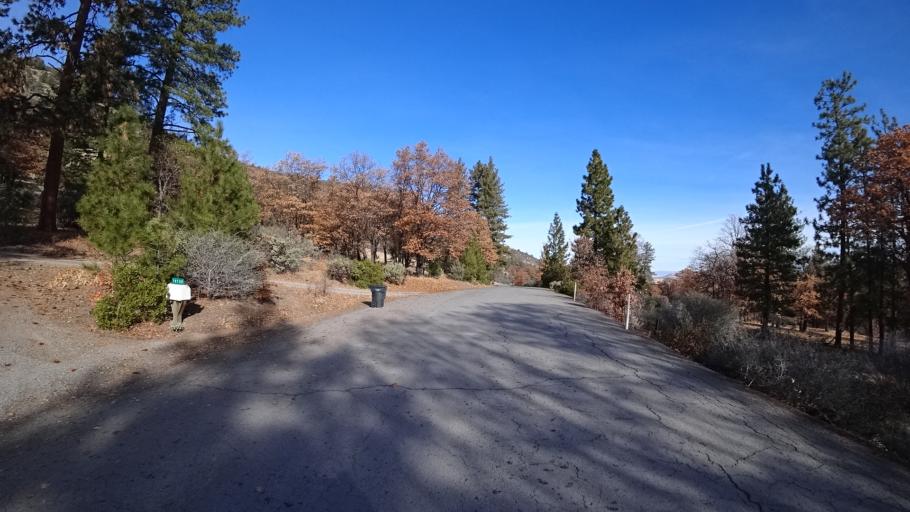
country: US
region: California
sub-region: Siskiyou County
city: Montague
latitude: 41.6167
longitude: -122.5780
